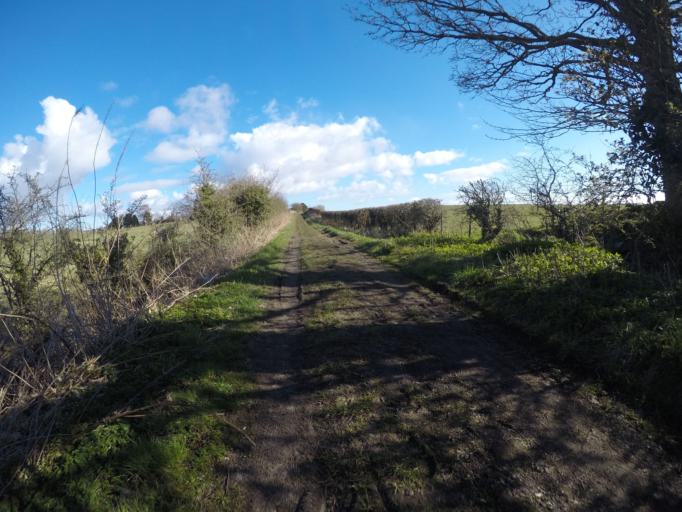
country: GB
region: Scotland
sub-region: North Ayrshire
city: Irvine
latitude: 55.6497
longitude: -4.6587
